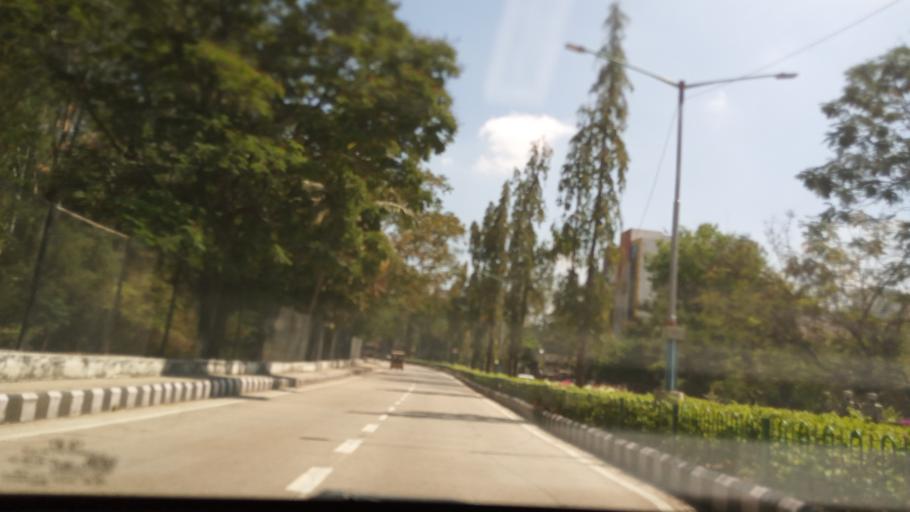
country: IN
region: Andhra Pradesh
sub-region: Chittoor
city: Akkarampalle
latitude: 13.6522
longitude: 79.4176
